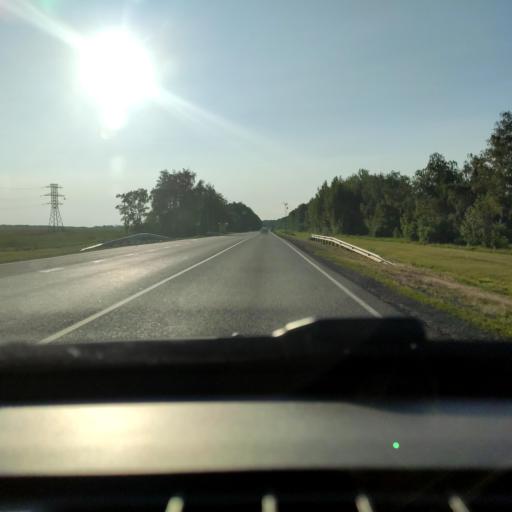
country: RU
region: Voronezj
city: Kashirskoye
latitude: 51.4782
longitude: 39.6705
